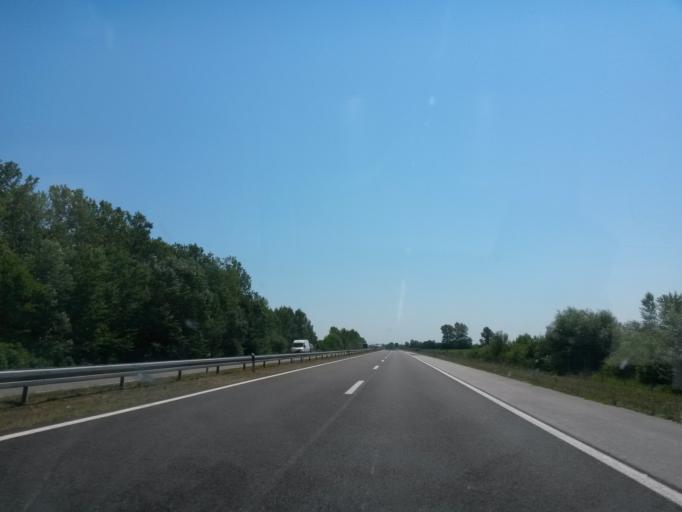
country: BA
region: Federation of Bosnia and Herzegovina
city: Donja Dubica
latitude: 45.1368
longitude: 18.3804
